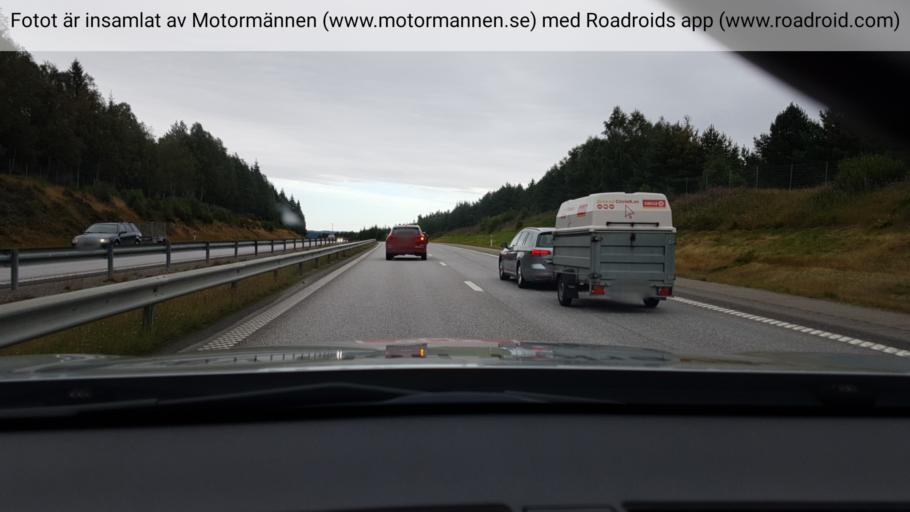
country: SE
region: Vaestra Goetaland
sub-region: Harryda Kommun
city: Hindas
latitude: 57.6701
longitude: 12.4342
